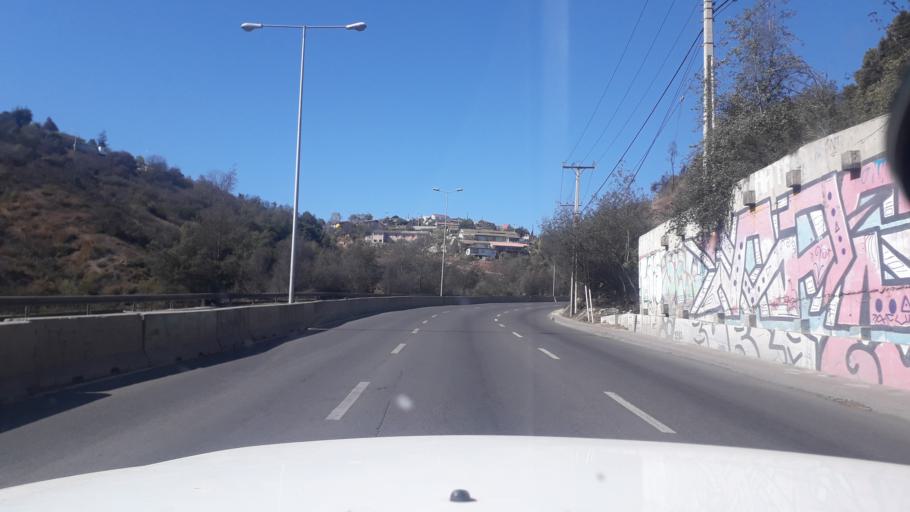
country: CL
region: Valparaiso
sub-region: Provincia de Valparaiso
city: Vina del Mar
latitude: -33.0354
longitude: -71.5126
